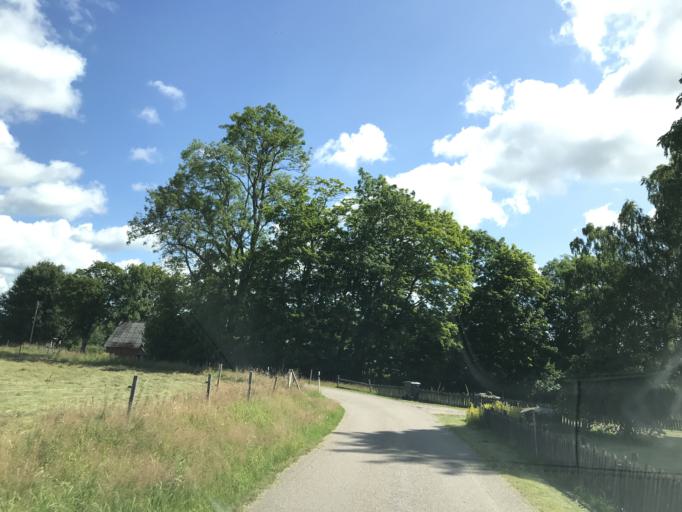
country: SE
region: Halland
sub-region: Laholms Kommun
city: Knared
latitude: 56.5113
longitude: 13.2976
